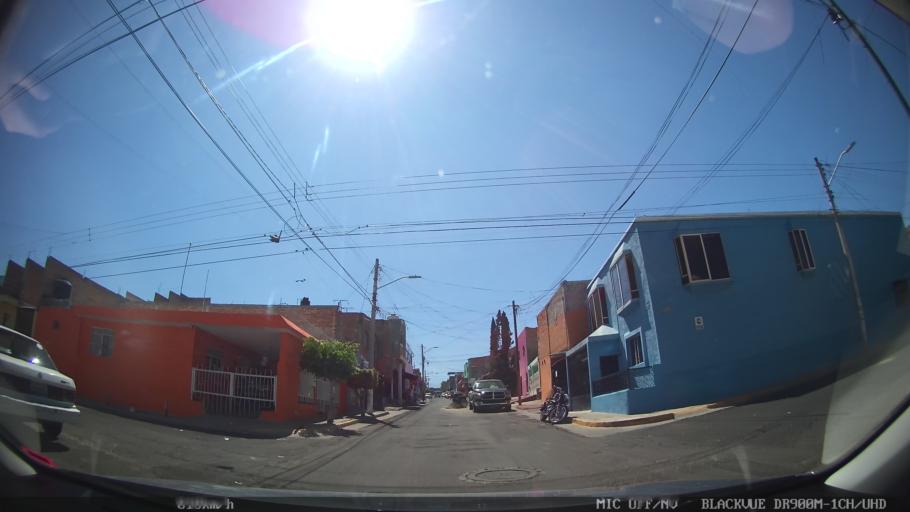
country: MX
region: Jalisco
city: Tlaquepaque
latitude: 20.6960
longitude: -103.2835
